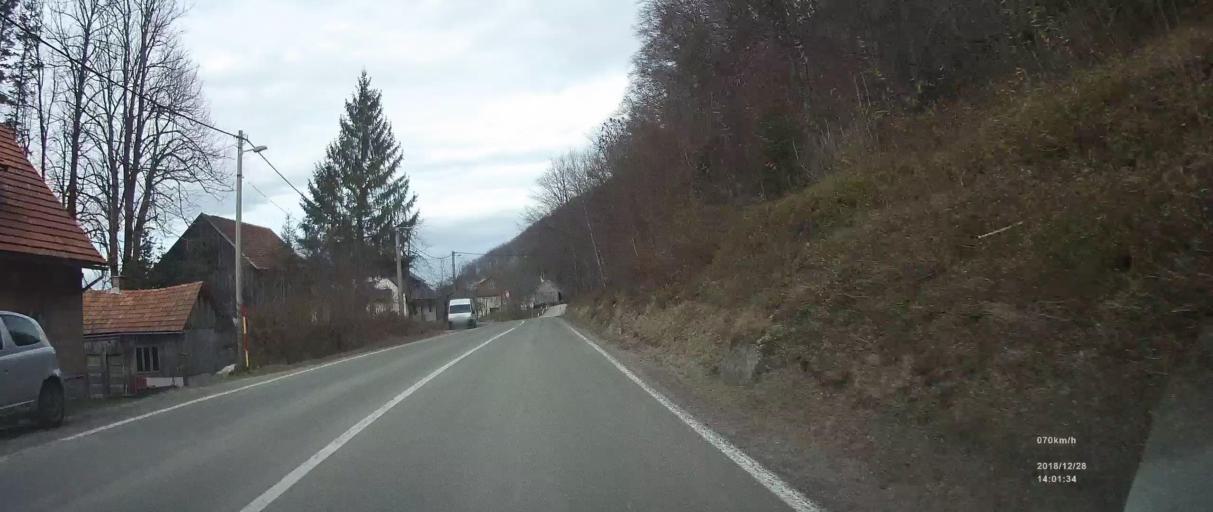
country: SI
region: Kostel
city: Kostel
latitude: 45.4213
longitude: 14.9071
